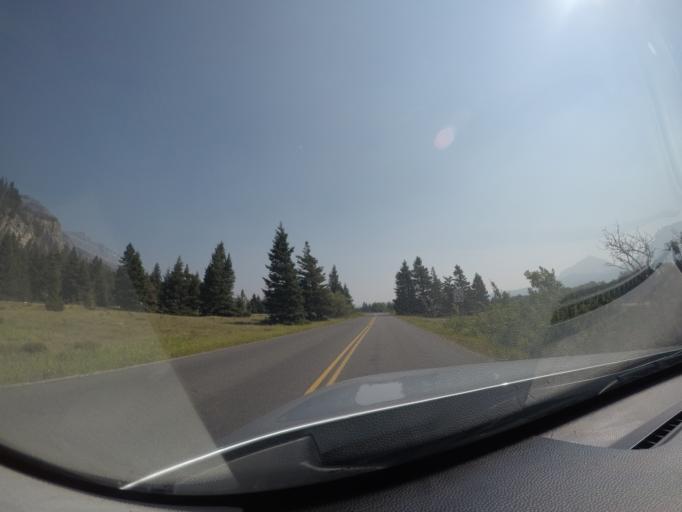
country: US
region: Montana
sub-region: Glacier County
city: Browning
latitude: 48.6918
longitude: -113.5241
